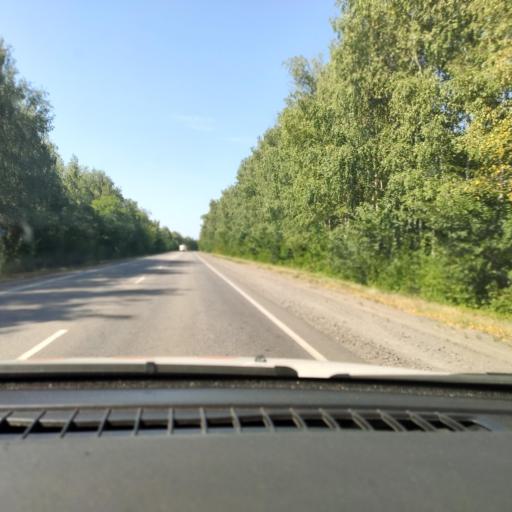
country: RU
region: Voronezj
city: Imeni Pervogo Maya
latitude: 50.7365
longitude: 39.3901
